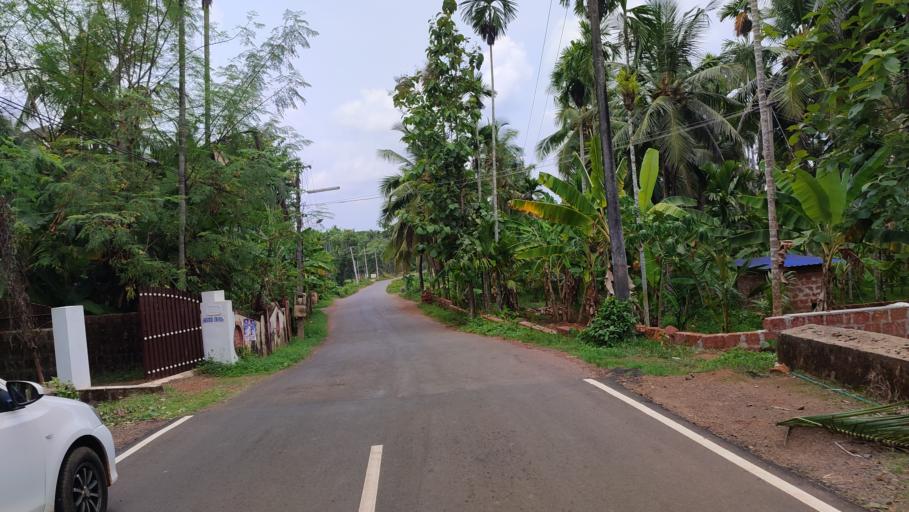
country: IN
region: Kerala
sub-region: Kasaragod District
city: Kannangad
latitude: 12.3206
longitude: 75.1113
